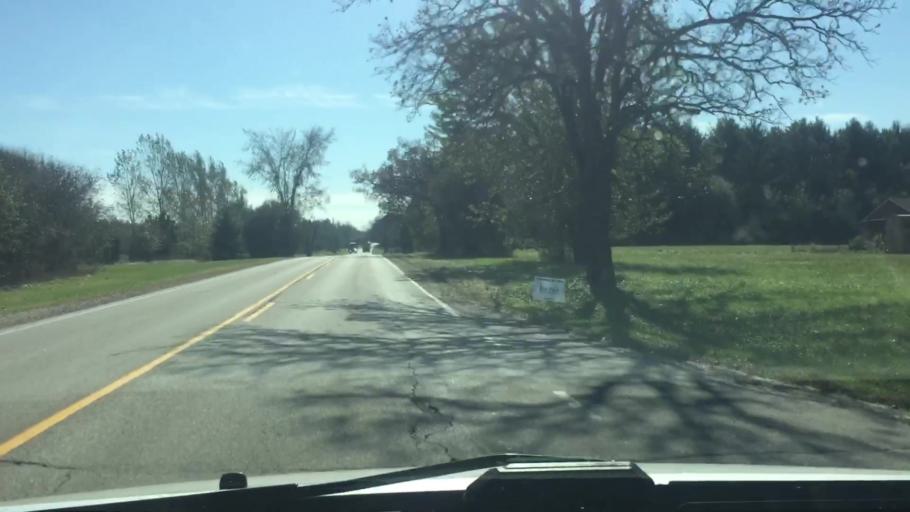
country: US
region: Wisconsin
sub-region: Waukesha County
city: North Prairie
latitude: 42.9640
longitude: -88.4049
